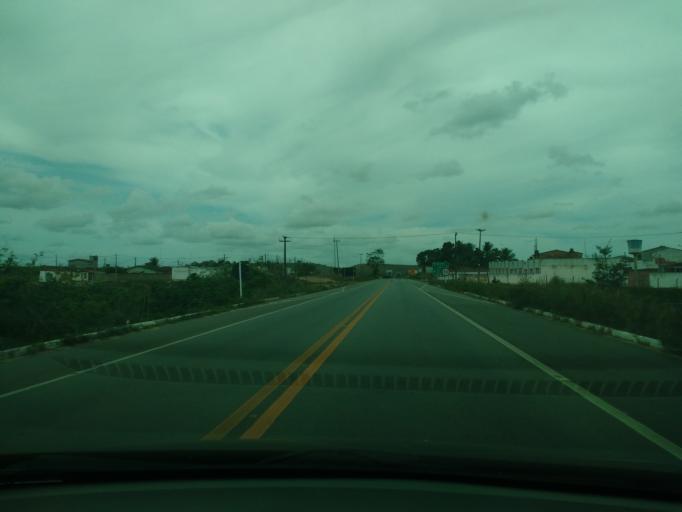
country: BR
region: Alagoas
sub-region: Murici
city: Murici
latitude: -9.3052
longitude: -35.9442
